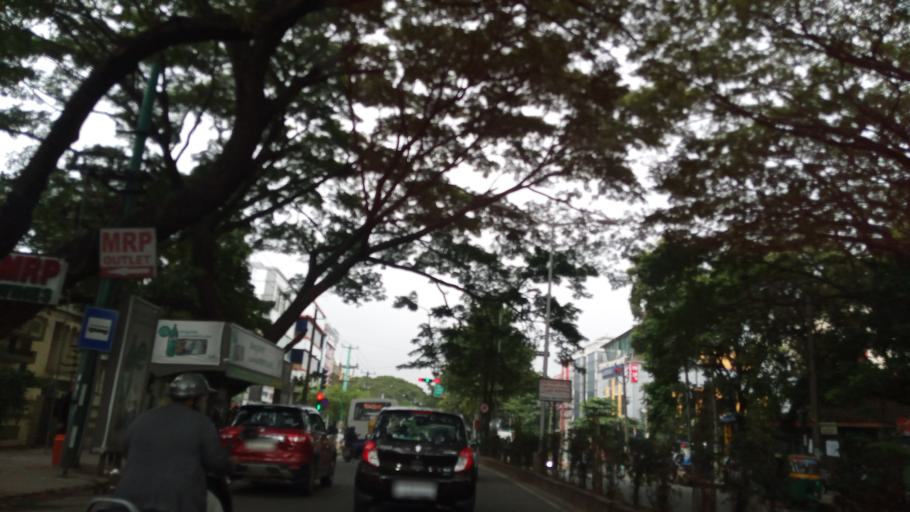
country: IN
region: Karnataka
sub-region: Bangalore Urban
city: Bangalore
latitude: 12.9284
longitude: 77.5458
